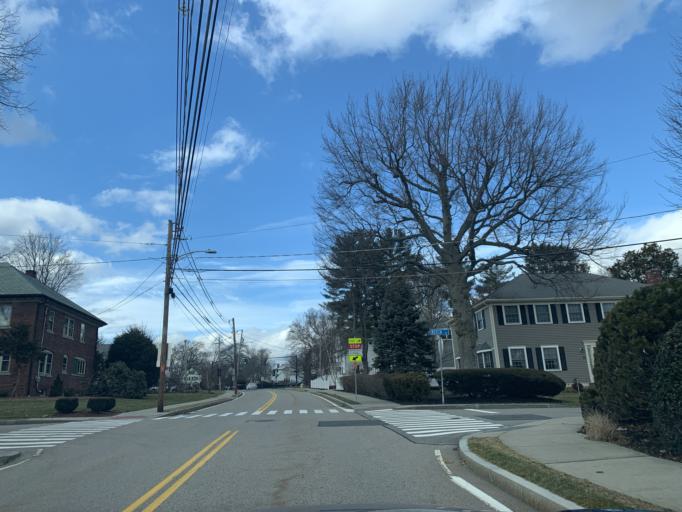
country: US
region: Massachusetts
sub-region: Norfolk County
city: Norwood
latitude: 42.1925
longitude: -71.2068
